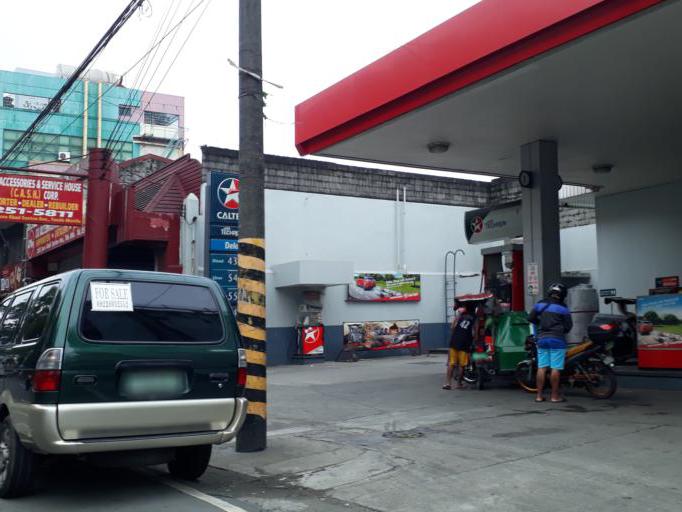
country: PH
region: Metro Manila
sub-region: City of Manila
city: Manila
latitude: 14.6227
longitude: 120.9781
